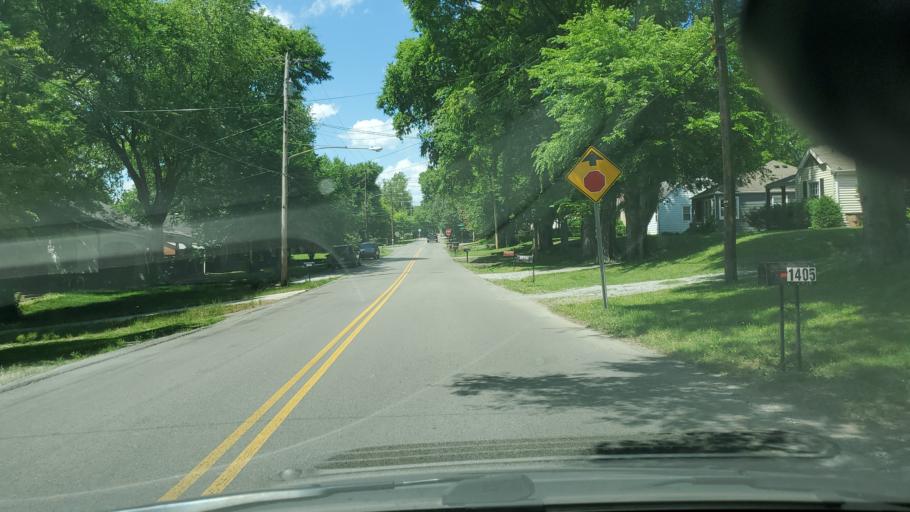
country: US
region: Tennessee
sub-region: Davidson County
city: Nashville
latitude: 36.1960
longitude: -86.7555
